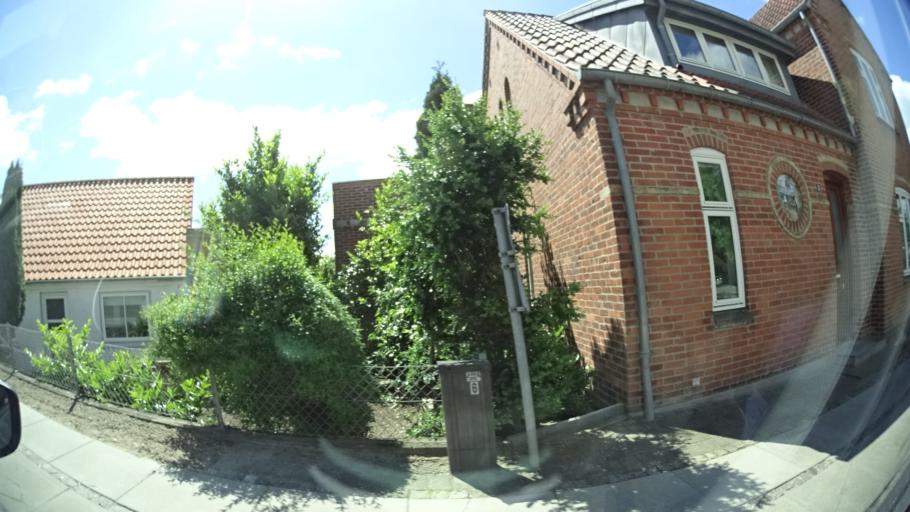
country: DK
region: Central Jutland
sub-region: Syddjurs Kommune
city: Ronde
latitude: 56.2995
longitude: 10.4814
